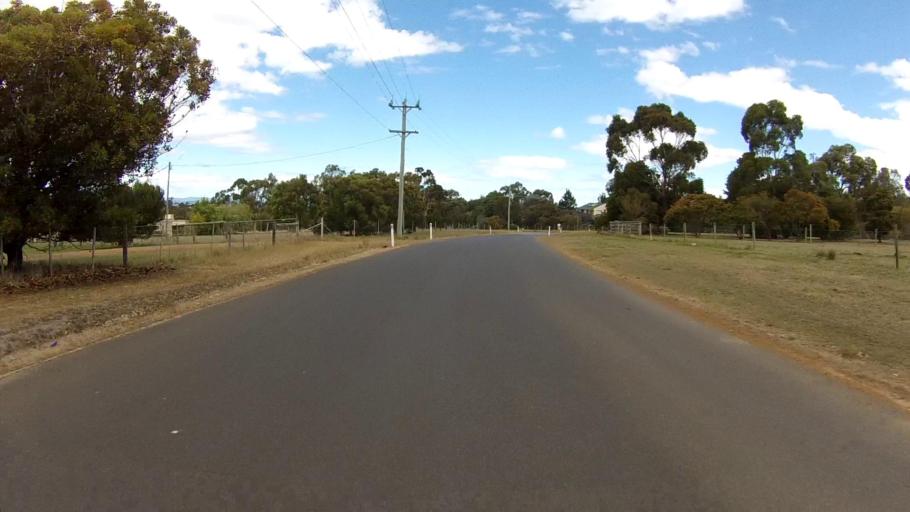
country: AU
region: Tasmania
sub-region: Clarence
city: Acton Park
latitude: -42.8837
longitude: 147.4790
